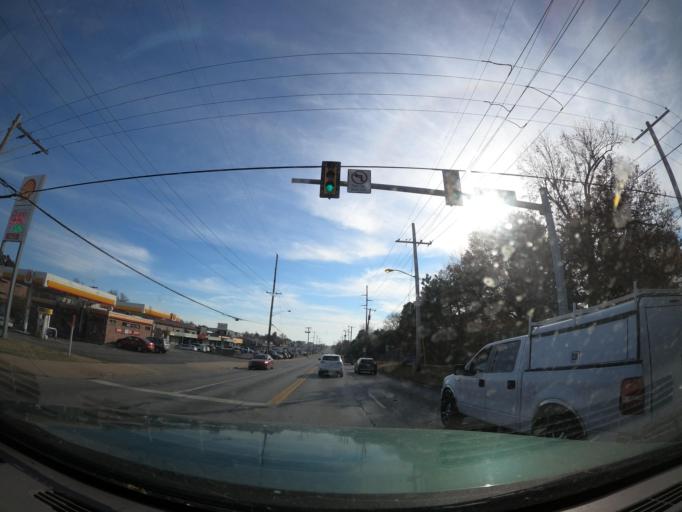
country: US
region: Oklahoma
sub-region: Tulsa County
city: Tulsa
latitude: 36.1116
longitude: -95.9403
